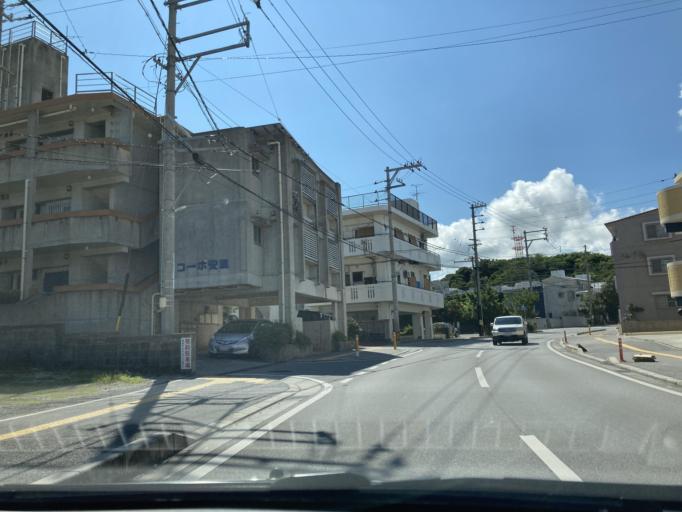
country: JP
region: Okinawa
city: Ginowan
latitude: 26.2205
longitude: 127.7327
